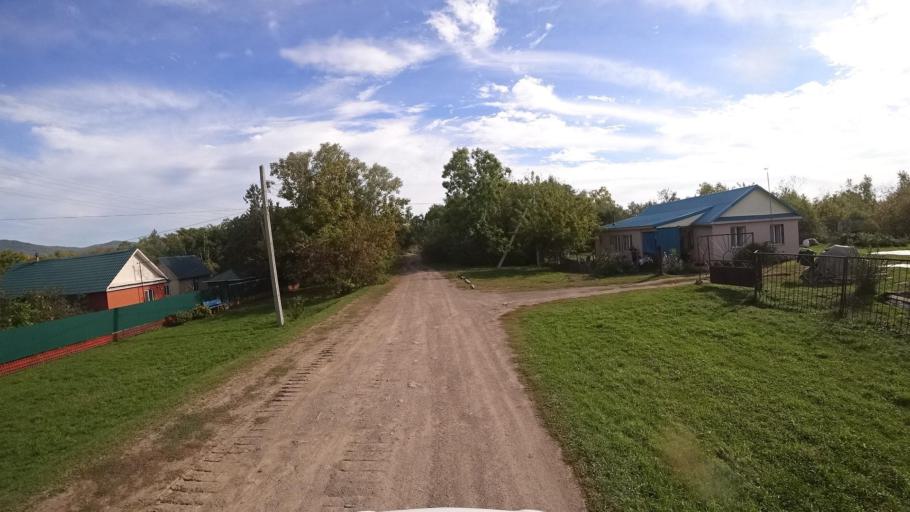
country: RU
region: Primorskiy
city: Dostoyevka
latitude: 44.2949
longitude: 133.4547
